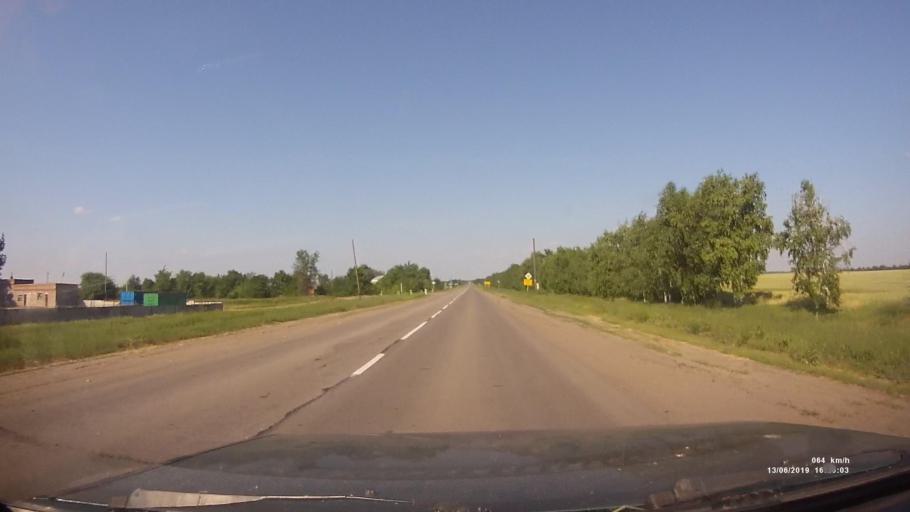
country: RU
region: Rostov
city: Kazanskaya
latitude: 49.8024
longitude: 41.1608
